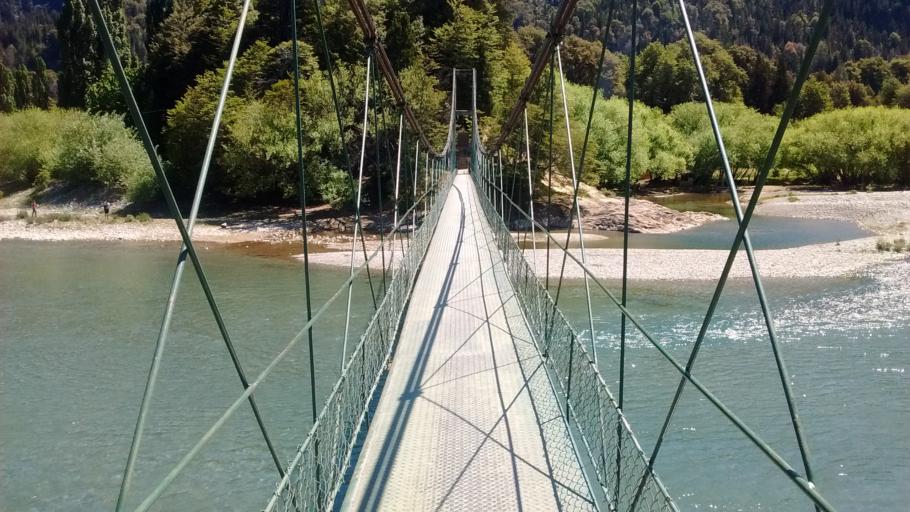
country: AR
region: Chubut
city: Lago Puelo
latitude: -42.0407
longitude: -71.6060
